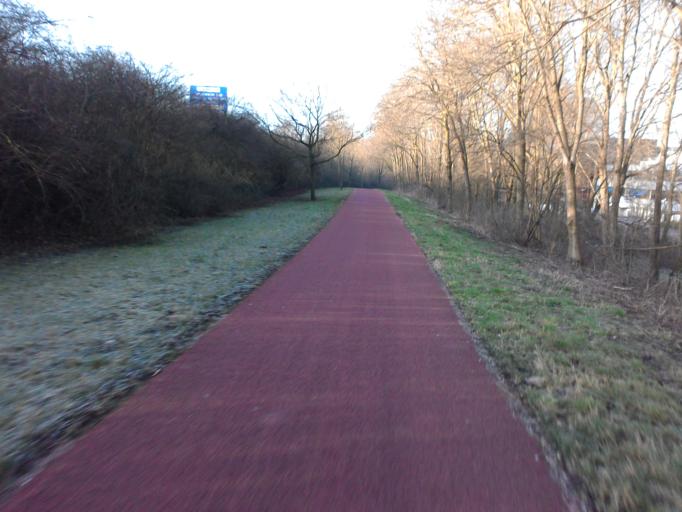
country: NL
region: Utrecht
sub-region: Stichtse Vecht
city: Maarssen
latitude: 52.1279
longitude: 5.0424
